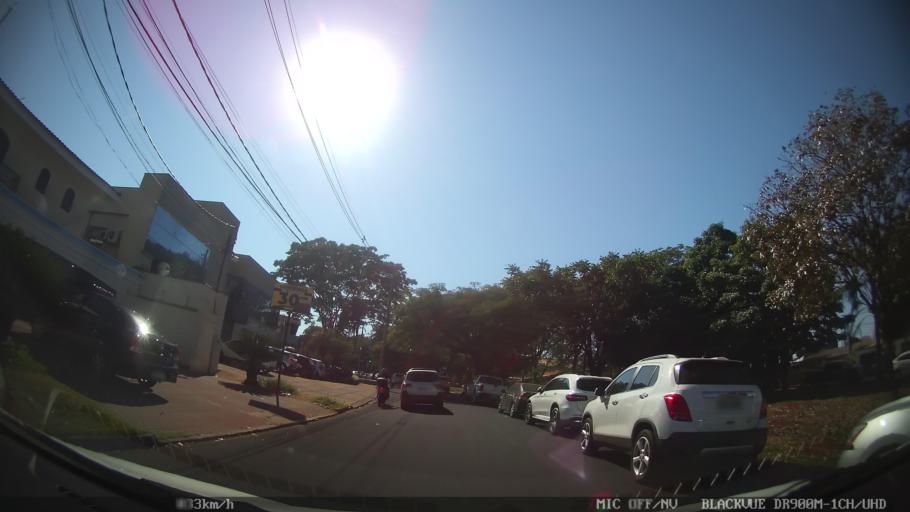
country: BR
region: Sao Paulo
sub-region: Ribeirao Preto
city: Ribeirao Preto
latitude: -21.2009
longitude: -47.8152
